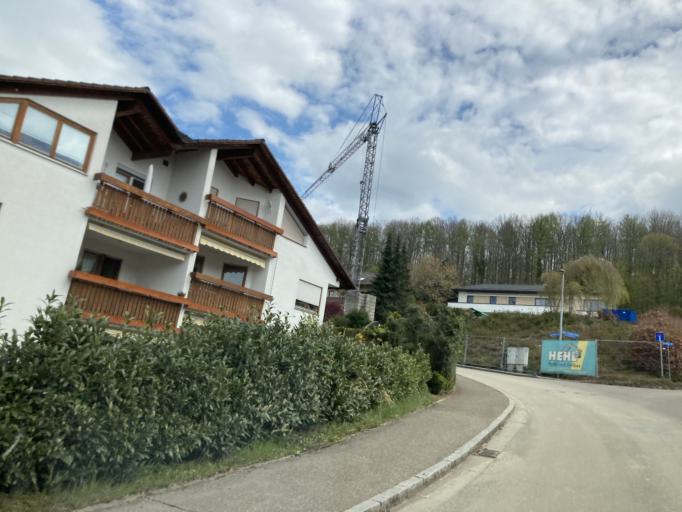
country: DE
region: Baden-Wuerttemberg
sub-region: Freiburg Region
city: Mullheim
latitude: 47.7993
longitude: 7.6279
